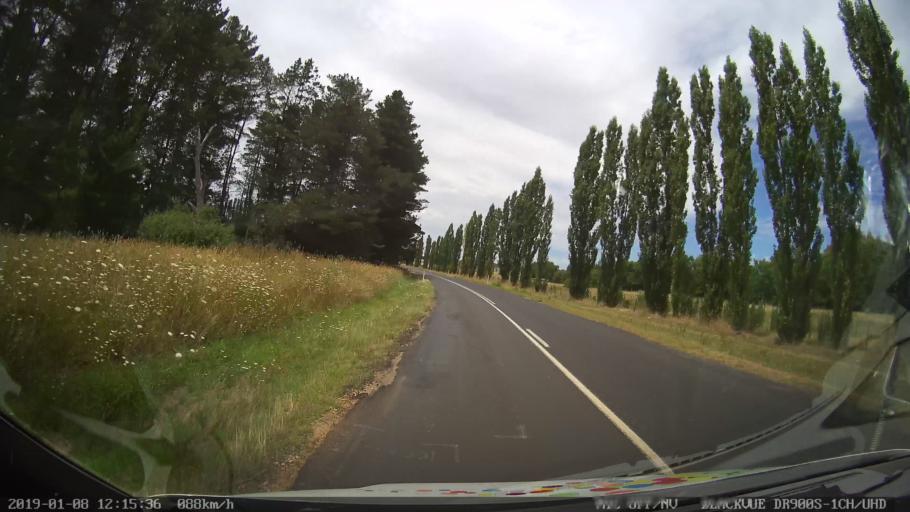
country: AU
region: New South Wales
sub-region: Armidale Dumaresq
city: Armidale
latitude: -30.4902
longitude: 151.6280
